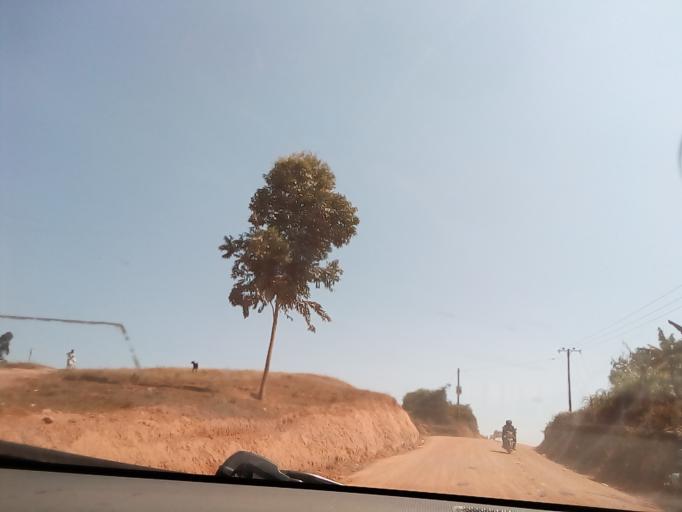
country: UG
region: Central Region
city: Masaka
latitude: -0.3664
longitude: 31.7492
